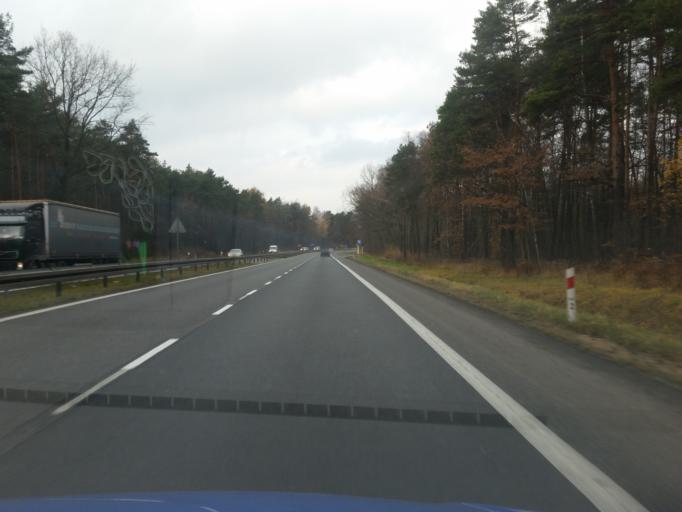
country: PL
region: Silesian Voivodeship
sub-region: Powiat myszkowski
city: Kozieglowy
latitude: 50.5380
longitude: 19.1857
